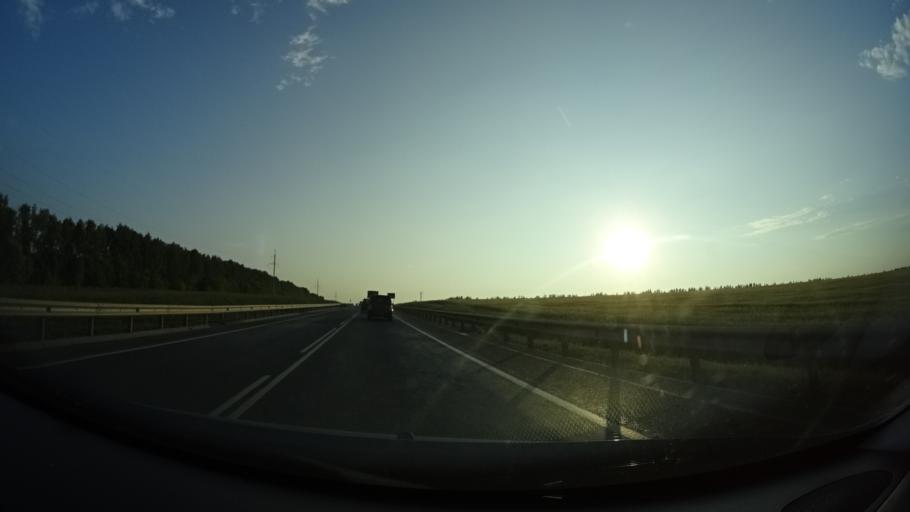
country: RU
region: Samara
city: Kamyshla
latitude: 54.0294
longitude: 51.9045
